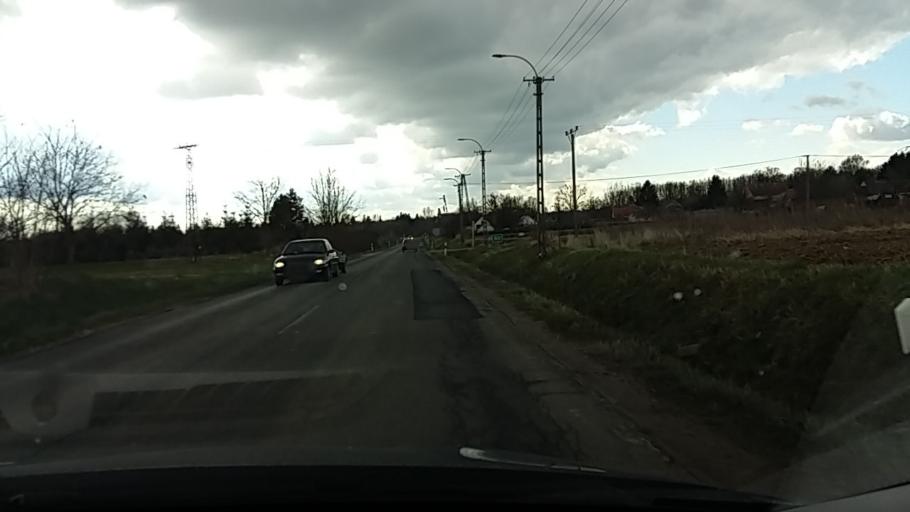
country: HU
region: Somogy
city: Bohonye
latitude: 46.4177
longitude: 17.3826
